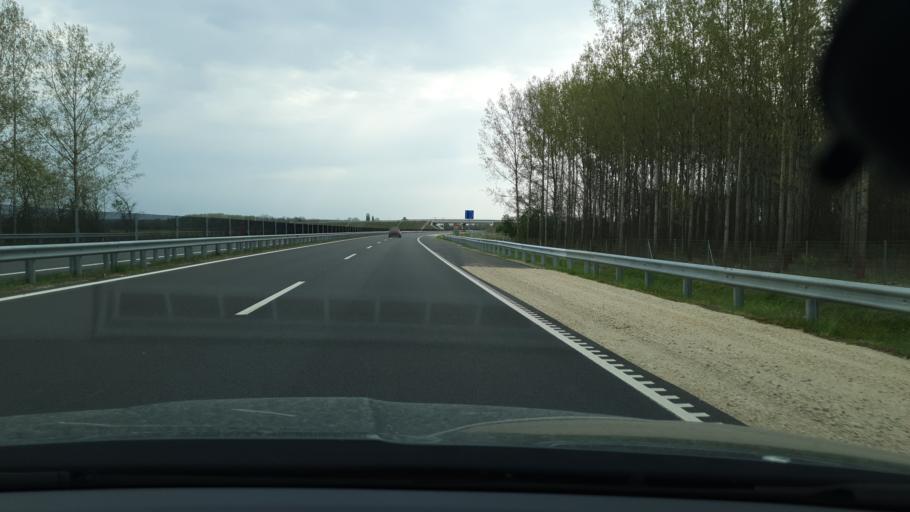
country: HU
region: Pest
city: Peteri
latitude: 47.3787
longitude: 19.3934
